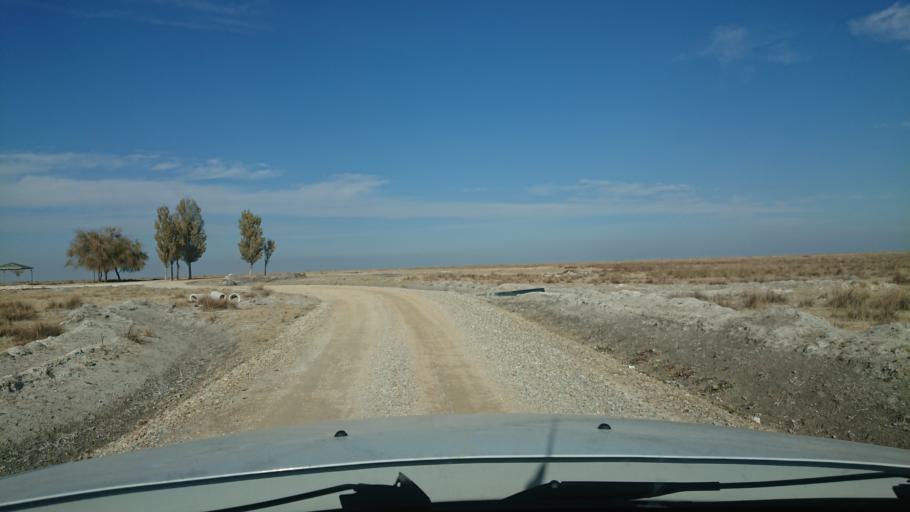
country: TR
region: Aksaray
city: Eskil
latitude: 38.4738
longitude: 33.4577
